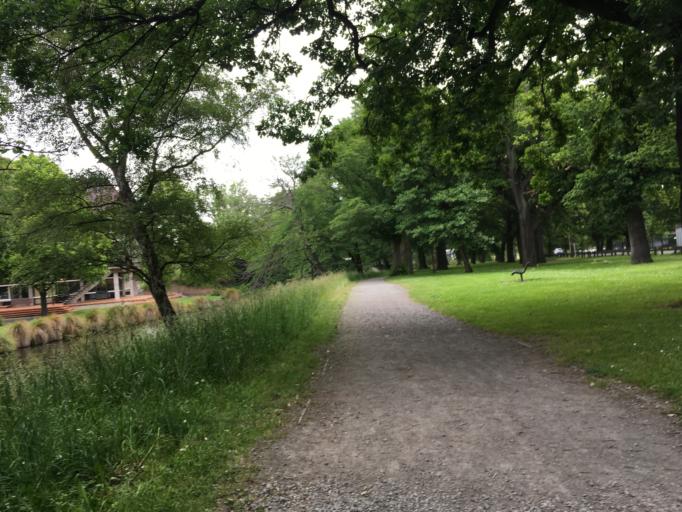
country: NZ
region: Canterbury
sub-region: Christchurch City
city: Christchurch
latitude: -43.5293
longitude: 172.6258
